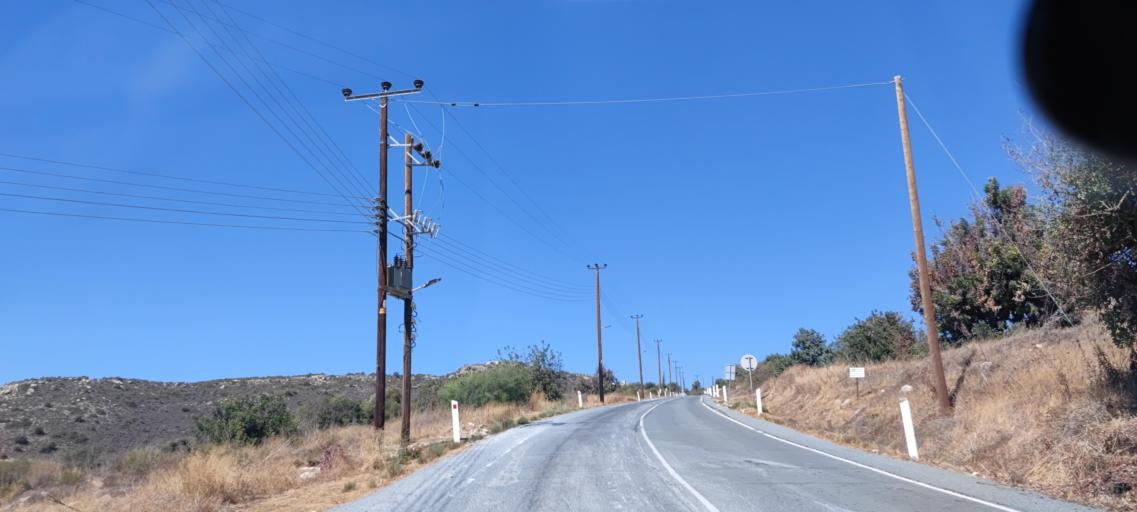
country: CY
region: Limassol
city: Mouttagiaka
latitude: 34.7454
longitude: 33.0594
